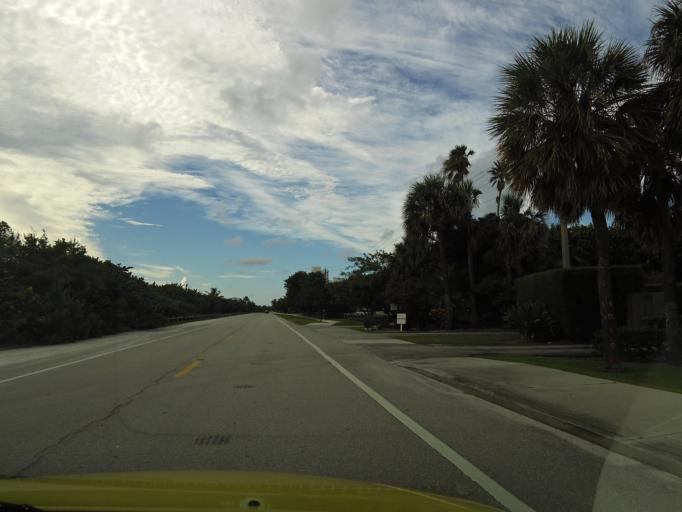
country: US
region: Florida
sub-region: Palm Beach County
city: Jupiter
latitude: 26.9617
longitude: -80.0788
